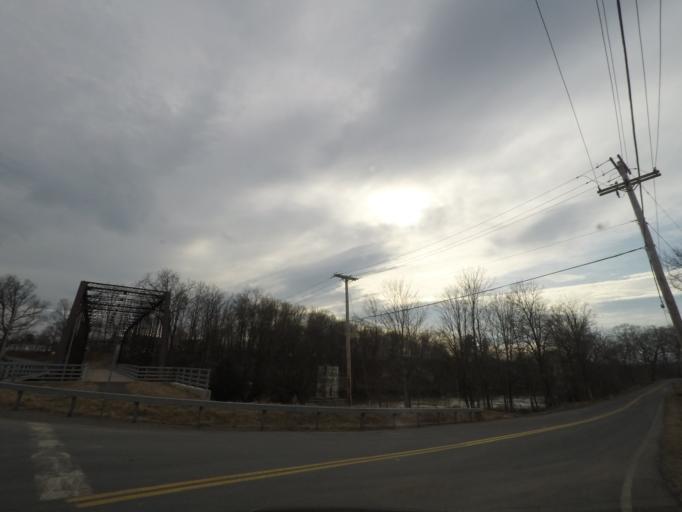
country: US
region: New York
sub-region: Saratoga County
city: Stillwater
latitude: 42.9185
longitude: -73.5140
